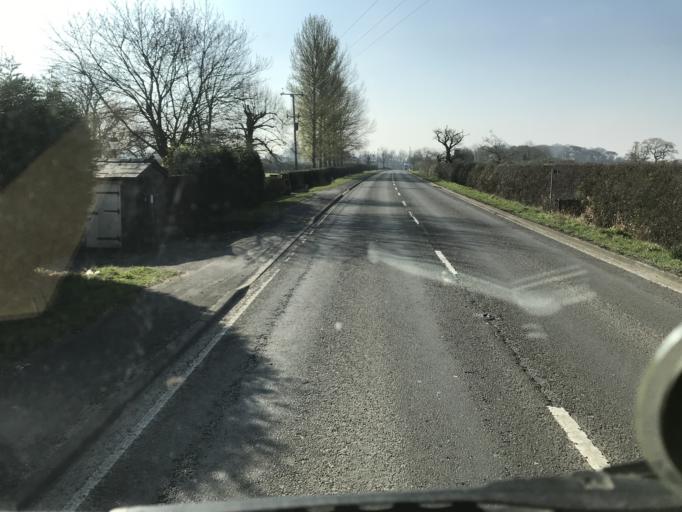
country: GB
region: England
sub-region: Cheshire West and Chester
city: Waverton
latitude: 53.1494
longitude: -2.8116
